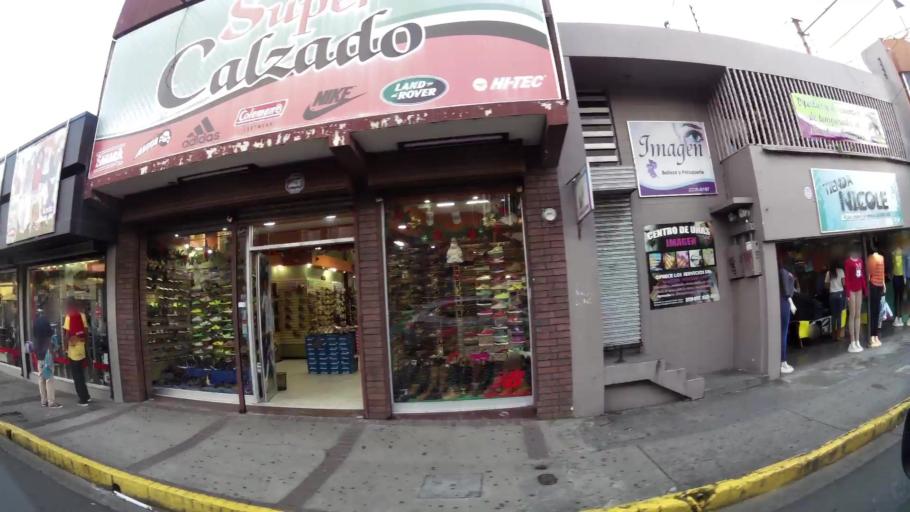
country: CR
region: Heredia
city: Heredia
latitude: 9.9971
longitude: -84.1169
